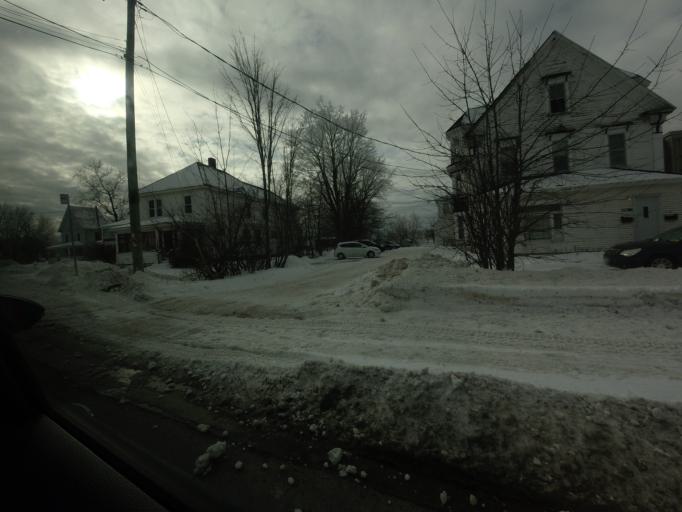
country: CA
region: New Brunswick
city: Fredericton
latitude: 45.9664
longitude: -66.6281
